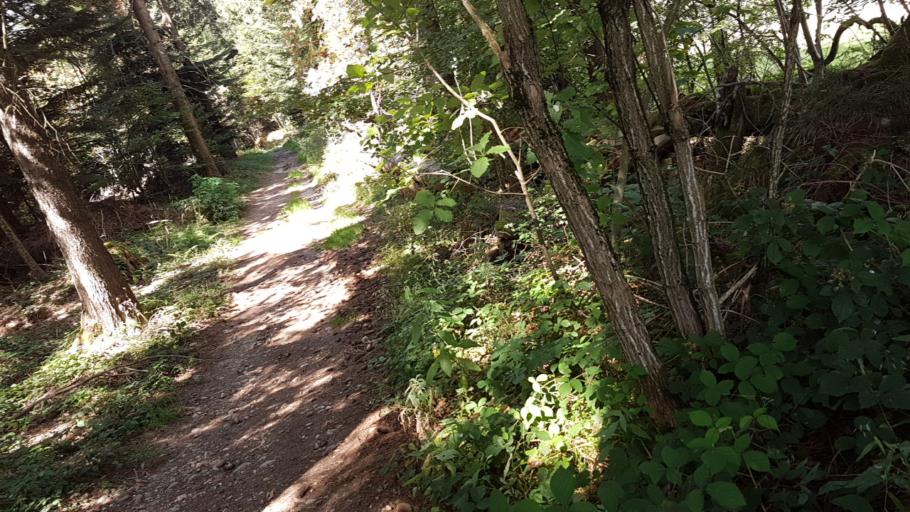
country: CH
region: Bern
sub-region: Thun District
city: Buchholterberg
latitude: 46.8249
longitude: 7.6578
